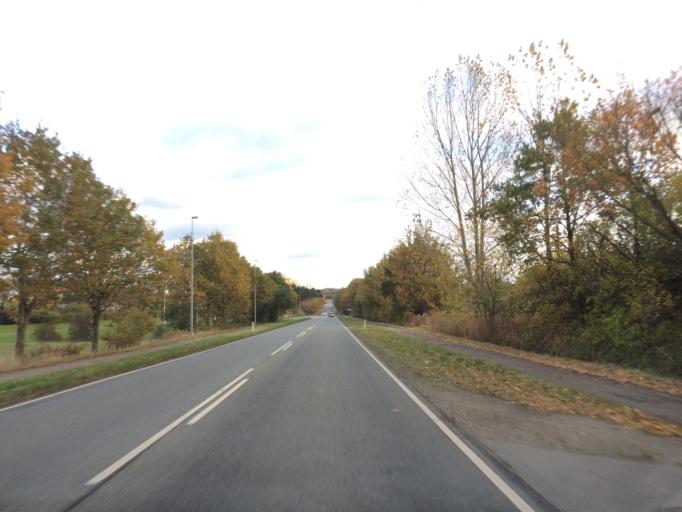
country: DK
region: South Denmark
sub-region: Sonderborg Kommune
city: Nordborg
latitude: 55.0395
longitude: 9.8044
